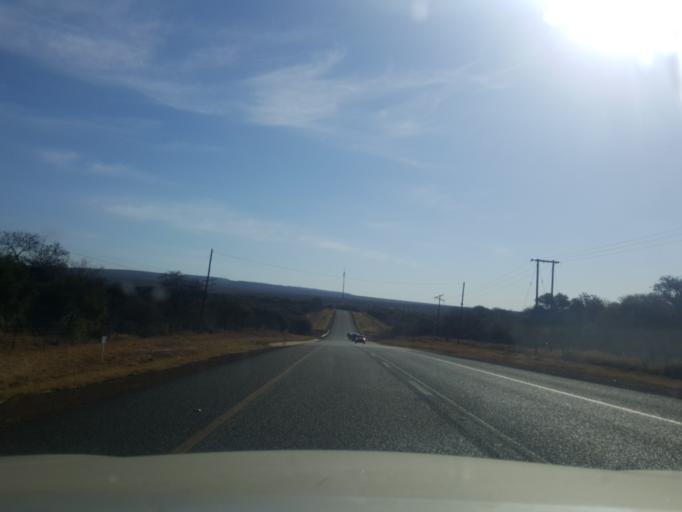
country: ZA
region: North-West
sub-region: Ngaka Modiri Molema District Municipality
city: Zeerust
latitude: -25.5197
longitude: 26.1745
